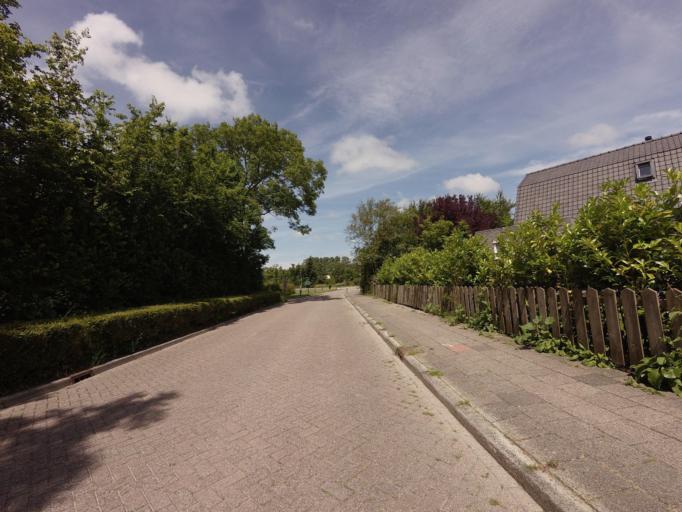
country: NL
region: North Holland
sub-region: Gemeente Texel
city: Den Burg
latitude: 53.0861
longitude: 4.8705
